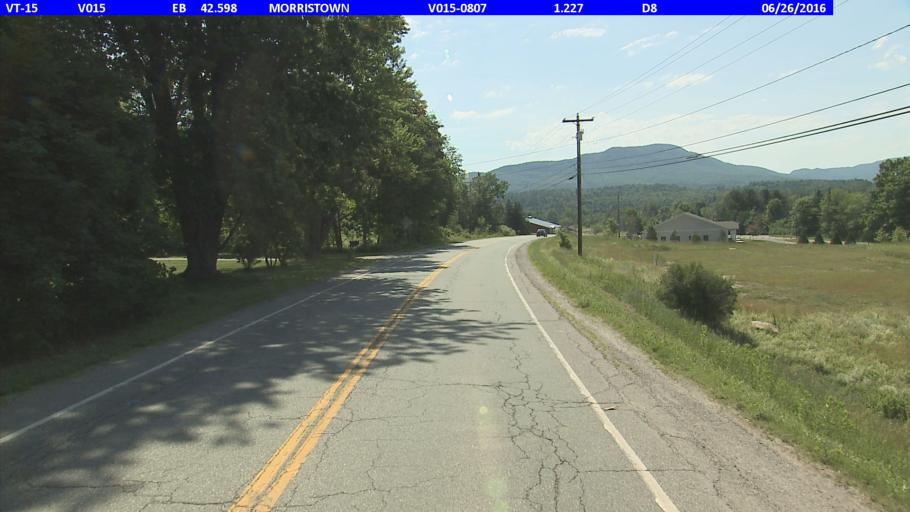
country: US
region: Vermont
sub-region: Lamoille County
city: Morrisville
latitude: 44.5725
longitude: -72.5871
